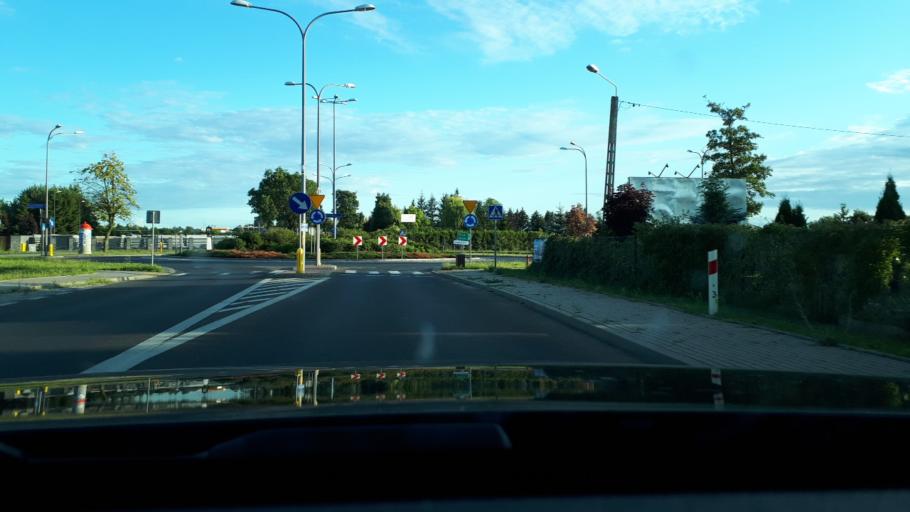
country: PL
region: Masovian Voivodeship
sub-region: Powiat ciechanowski
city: Ciechanow
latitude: 52.8462
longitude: 20.6225
